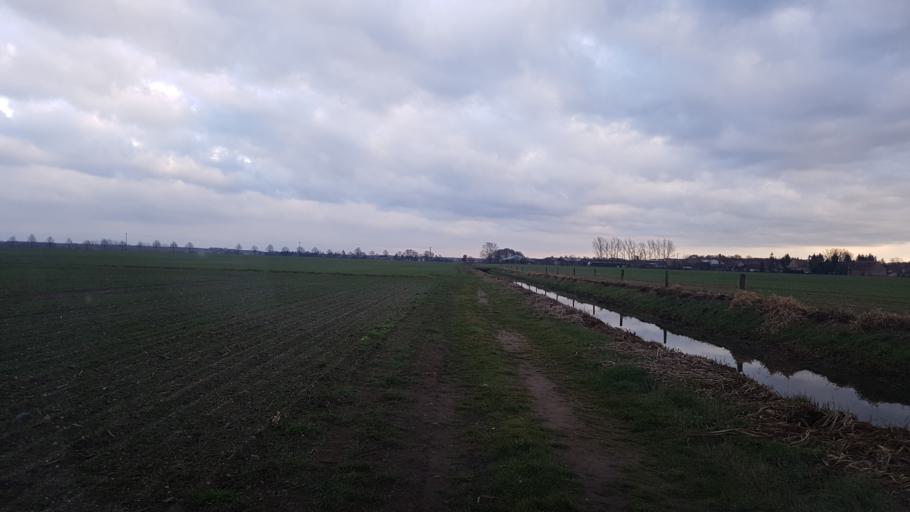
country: DE
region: Brandenburg
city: Schonborn
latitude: 51.5744
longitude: 13.5166
